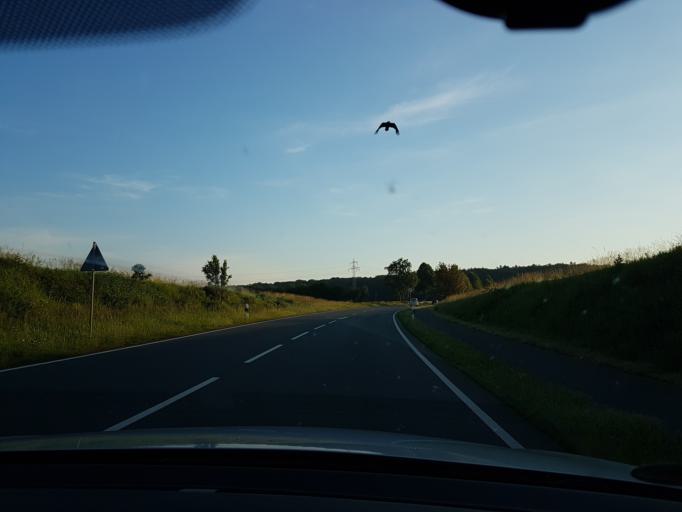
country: DE
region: Lower Saxony
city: Wolsdorf
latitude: 52.1975
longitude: 10.9677
